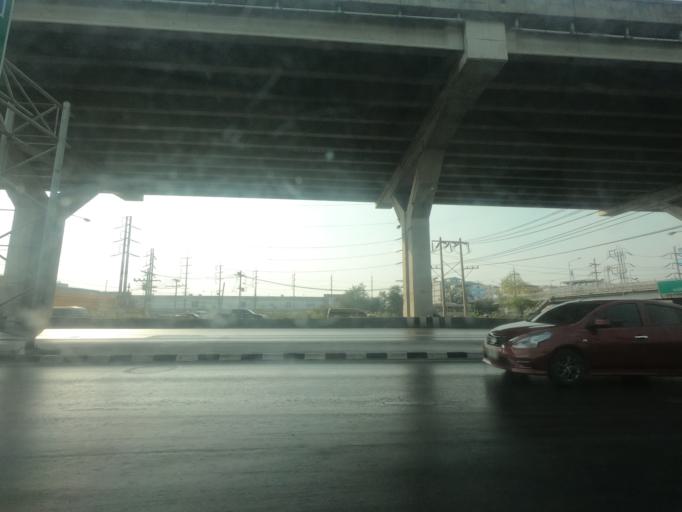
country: TH
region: Bangkok
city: Sai Mai
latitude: 13.9726
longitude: 100.6706
